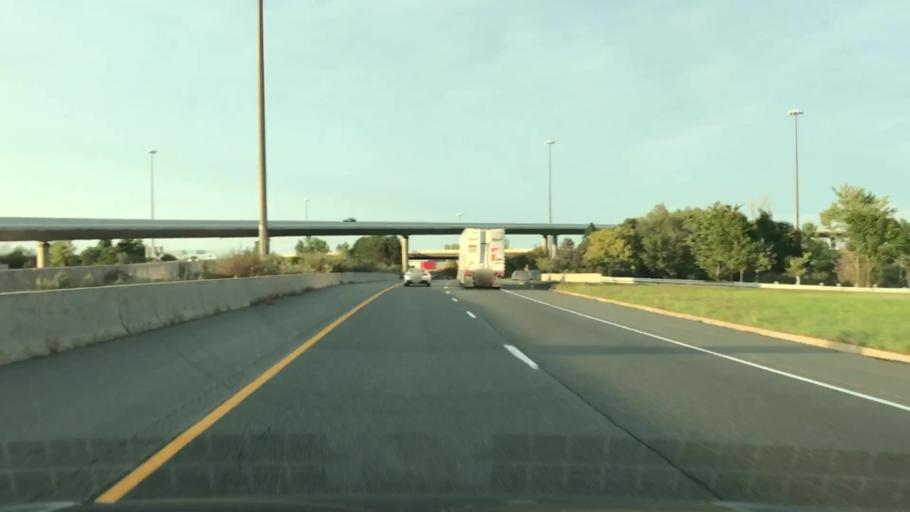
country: CA
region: Ontario
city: Niagara Falls
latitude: 43.0956
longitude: -79.1189
